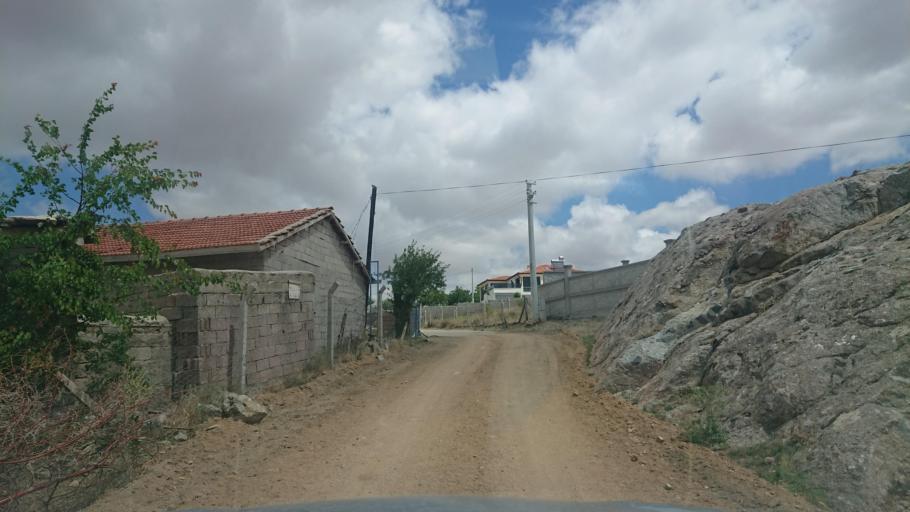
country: TR
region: Aksaray
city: Agacoren
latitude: 38.8673
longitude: 33.9471
